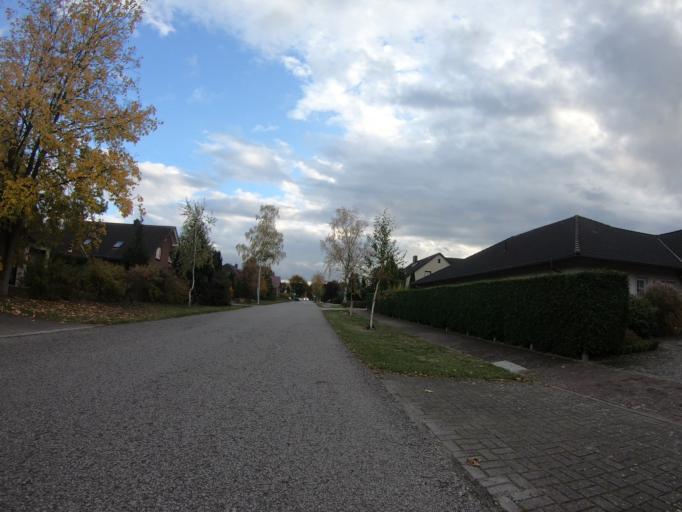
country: DE
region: Lower Saxony
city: Wagenhoff
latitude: 52.5537
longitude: 10.5265
